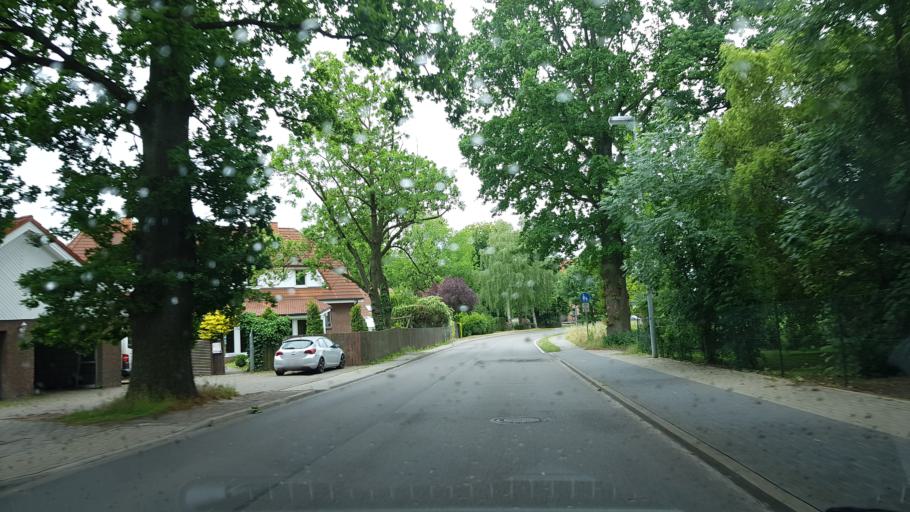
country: DE
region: Lower Saxony
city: Celle
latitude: 52.6521
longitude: 10.0582
